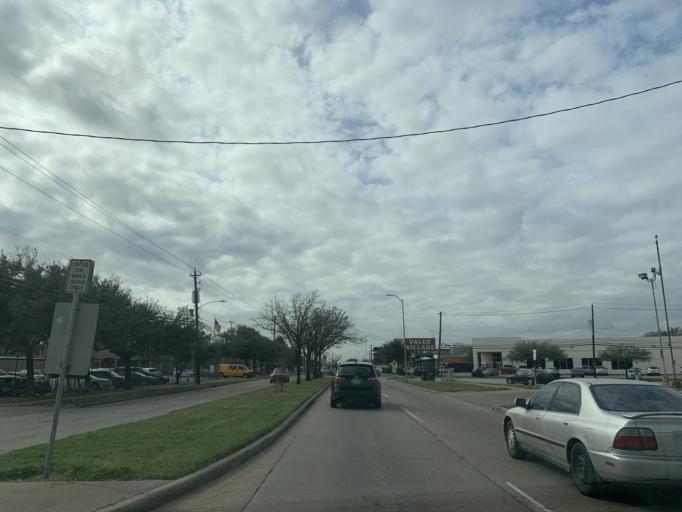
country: US
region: Texas
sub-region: Harris County
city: Bellaire
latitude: 29.6965
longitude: -95.4899
